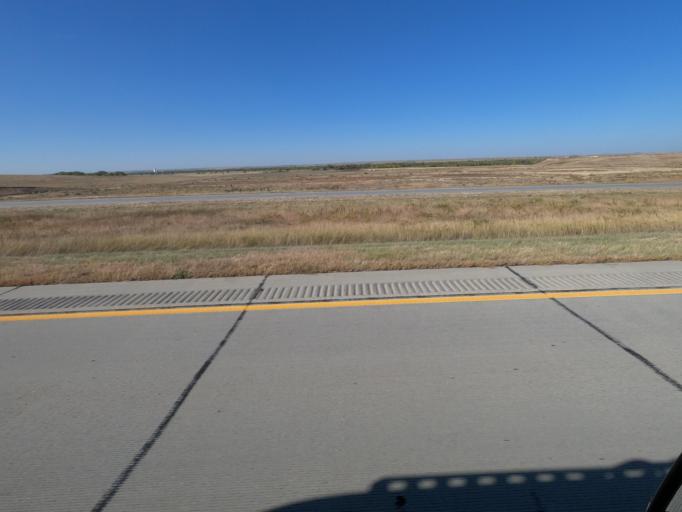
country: US
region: Colorado
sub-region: Sedgwick County
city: Julesburg
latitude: 40.9278
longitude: -102.3370
